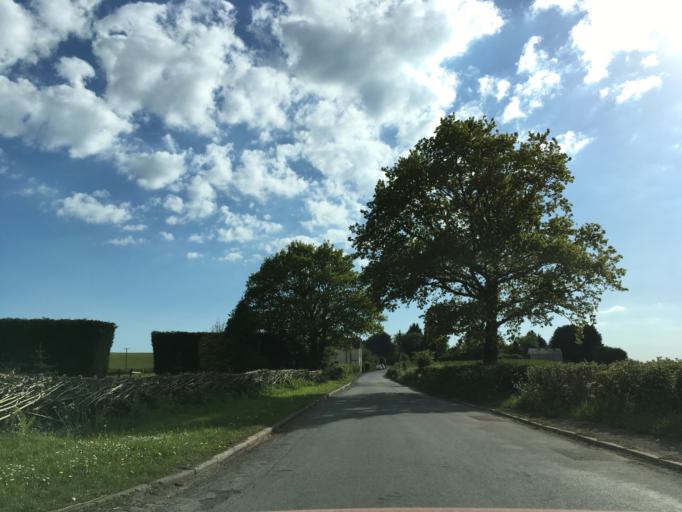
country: GB
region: Wales
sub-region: Newport
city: Marshfield
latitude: 51.5610
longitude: -3.0683
